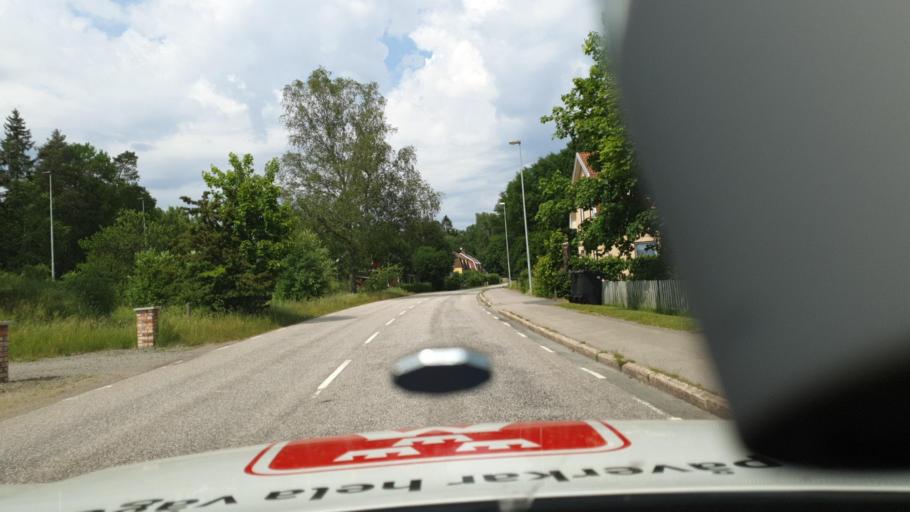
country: SE
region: Joenkoeping
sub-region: Varnamo Kommun
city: Varnamo
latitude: 57.2591
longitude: 14.0546
